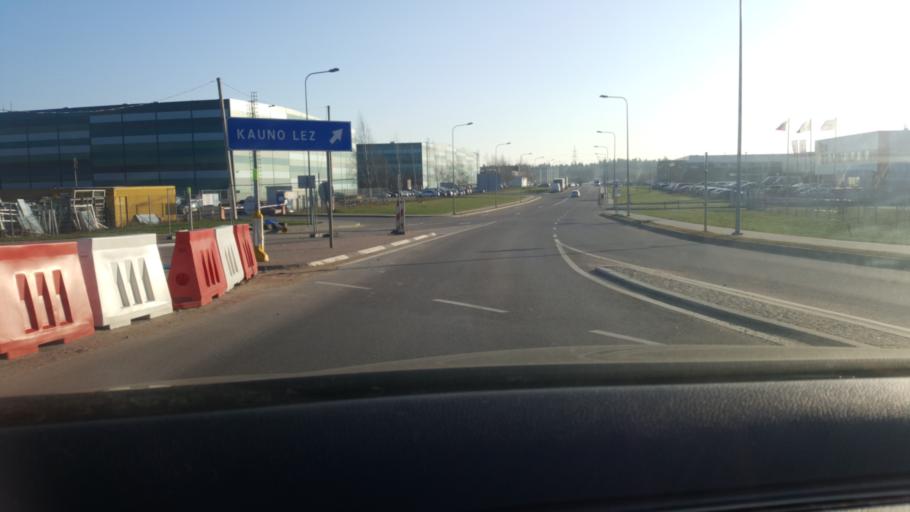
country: LT
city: Ramuciai
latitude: 54.9417
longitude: 24.0085
